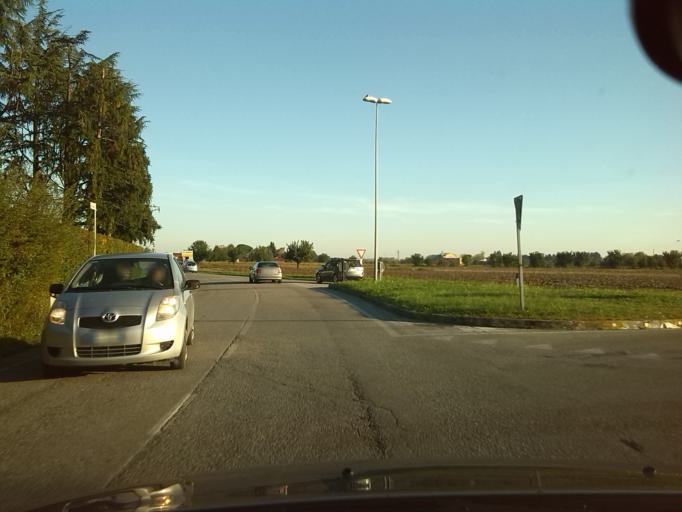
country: IT
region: Friuli Venezia Giulia
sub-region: Provincia di Udine
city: Pagnacco
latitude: 46.0985
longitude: 13.1792
